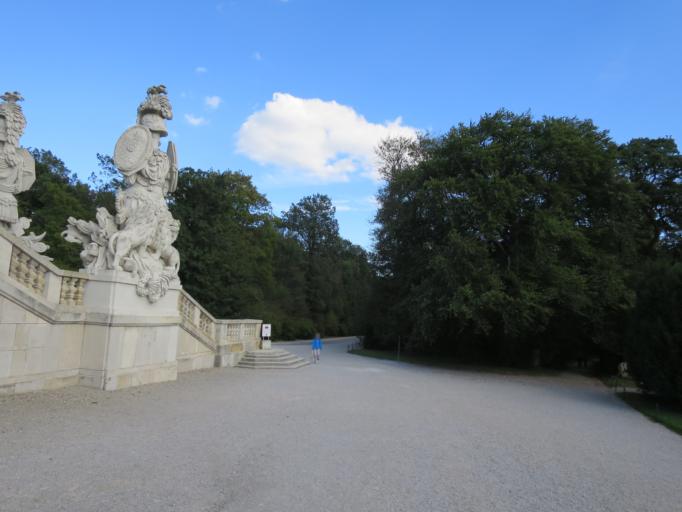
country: AT
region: Lower Austria
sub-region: Politischer Bezirk Modling
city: Vosendorf
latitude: 48.1781
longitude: 16.3092
